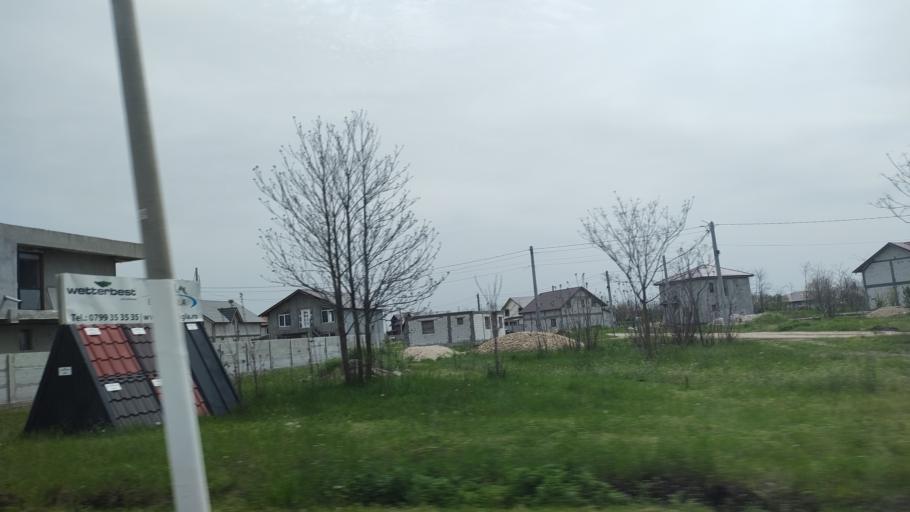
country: RO
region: Constanta
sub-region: Comuna Cobadin
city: Cobadin
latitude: 44.0725
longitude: 28.2350
